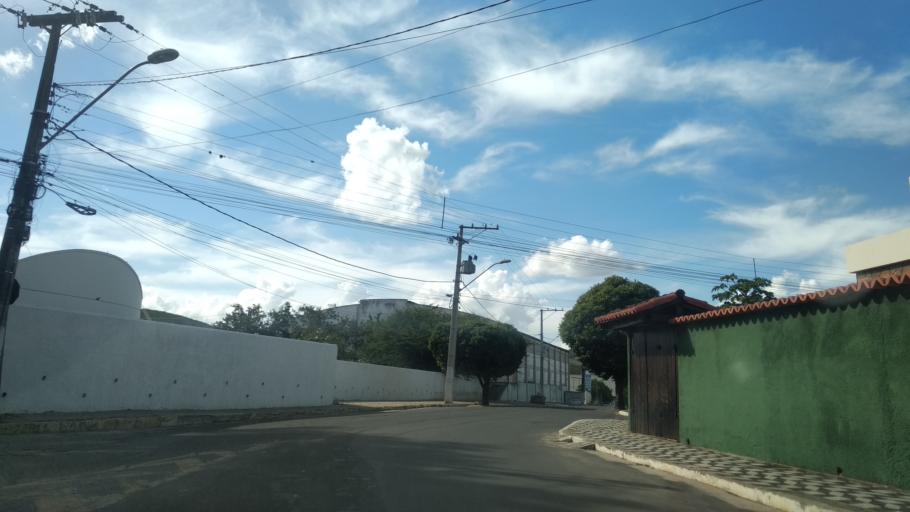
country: BR
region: Bahia
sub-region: Caetite
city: Caetite
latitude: -14.0685
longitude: -42.4924
